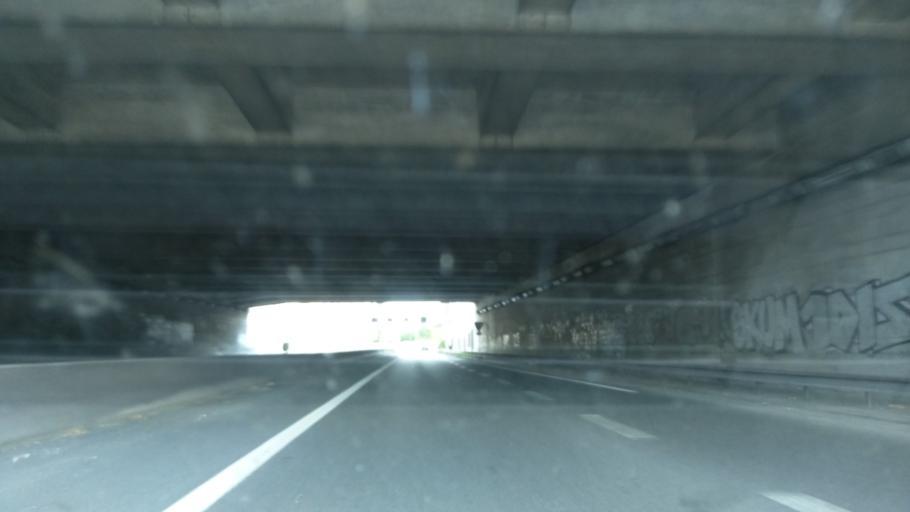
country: FR
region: Ile-de-France
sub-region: Departement des Yvelines
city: Chatou
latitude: 48.8883
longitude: 2.1678
